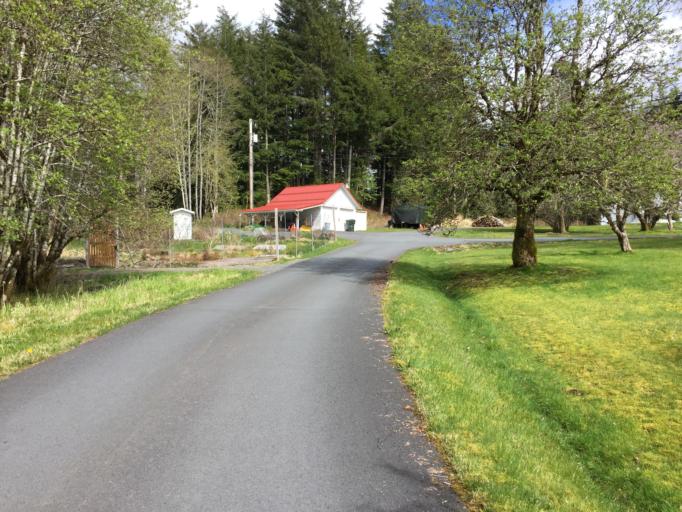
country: US
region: Alaska
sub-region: Sitka City and Borough
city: Sitka
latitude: 57.0560
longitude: -135.3268
